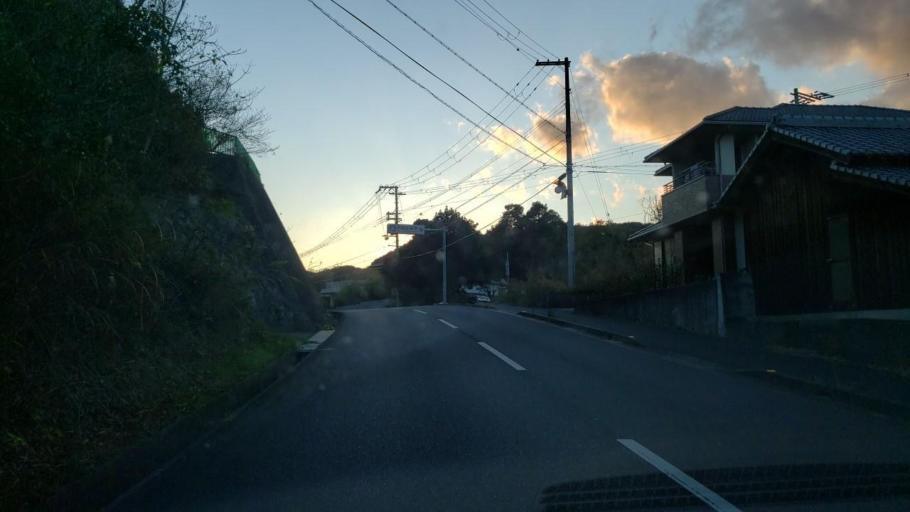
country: JP
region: Hyogo
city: Sumoto
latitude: 34.3599
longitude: 134.7859
